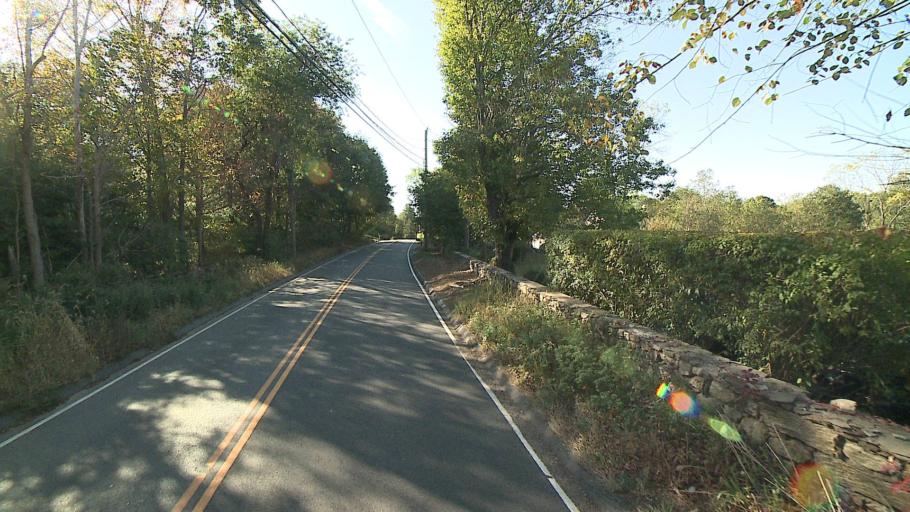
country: US
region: Connecticut
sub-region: Fairfield County
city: Westport
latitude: 41.1697
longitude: -73.3946
